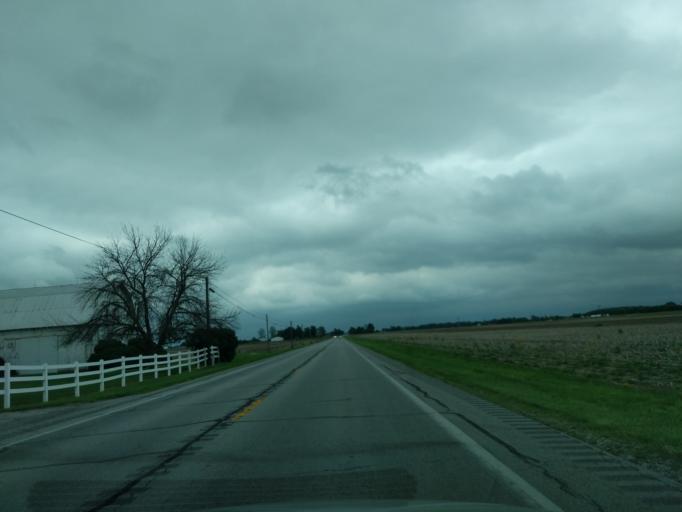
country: US
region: Indiana
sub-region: Madison County
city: Frankton
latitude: 40.2775
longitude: -85.7841
